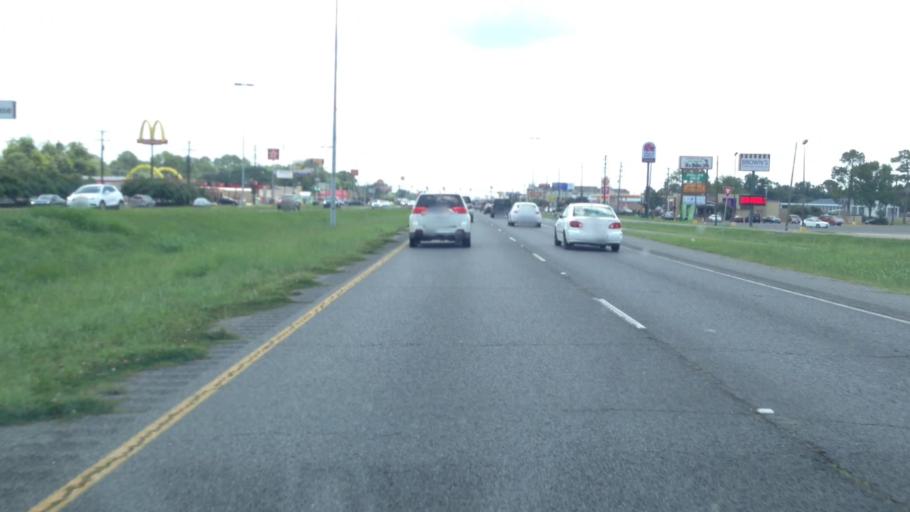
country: US
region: Louisiana
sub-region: Rapides Parish
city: Alexandria
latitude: 31.2979
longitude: -92.4796
